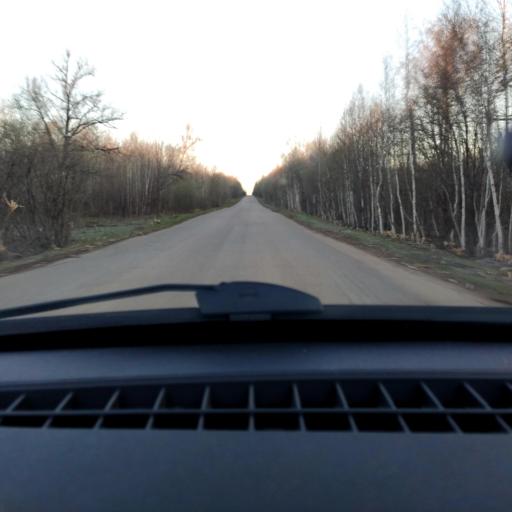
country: RU
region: Bashkortostan
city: Chishmy
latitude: 54.4433
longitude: 55.5558
